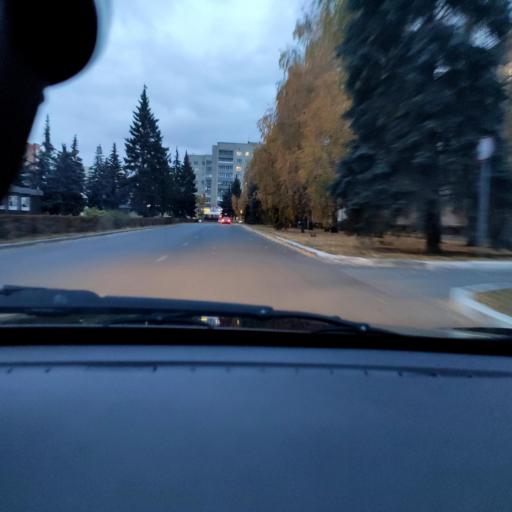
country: RU
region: Samara
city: Tol'yatti
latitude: 53.5075
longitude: 49.4185
